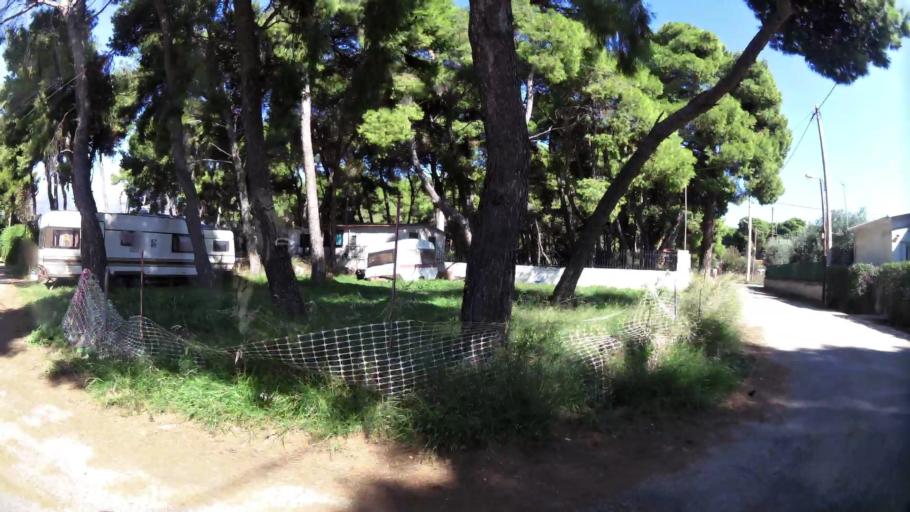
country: GR
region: Attica
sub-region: Nomarchia Athinas
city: Lykovrysi
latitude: 38.0831
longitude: 23.7768
